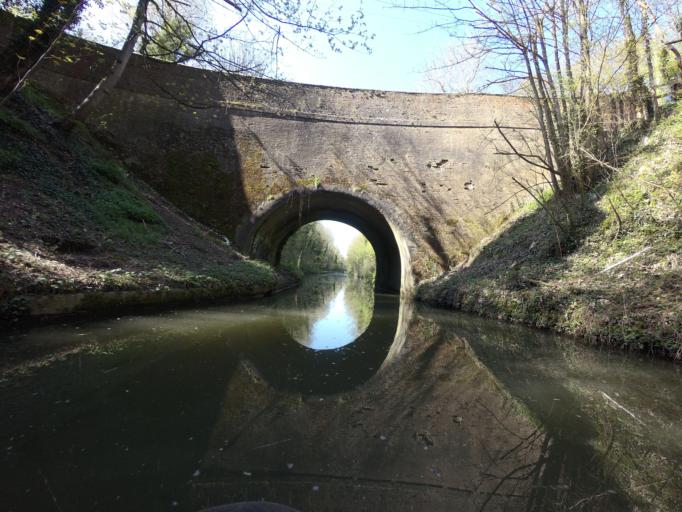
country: GB
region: England
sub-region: Hertfordshire
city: Tring
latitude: 51.8068
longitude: -0.6391
